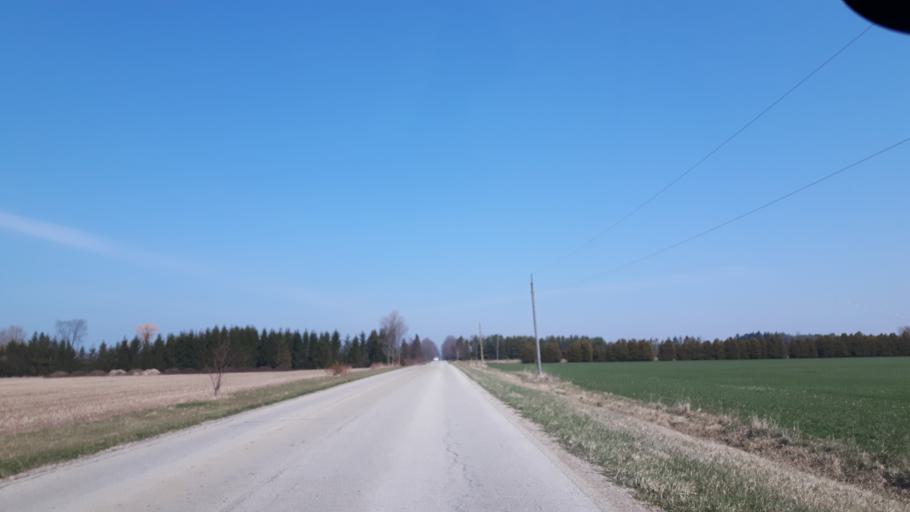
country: CA
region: Ontario
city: Goderich
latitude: 43.6481
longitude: -81.6845
